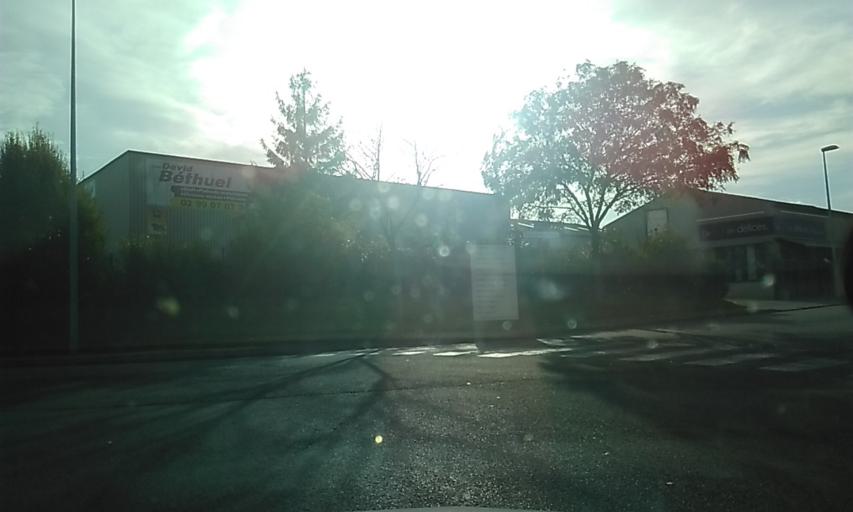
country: FR
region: Brittany
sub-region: Departement d'Ille-et-Vilaine
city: Pleumeleuc
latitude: 48.1796
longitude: -1.9199
